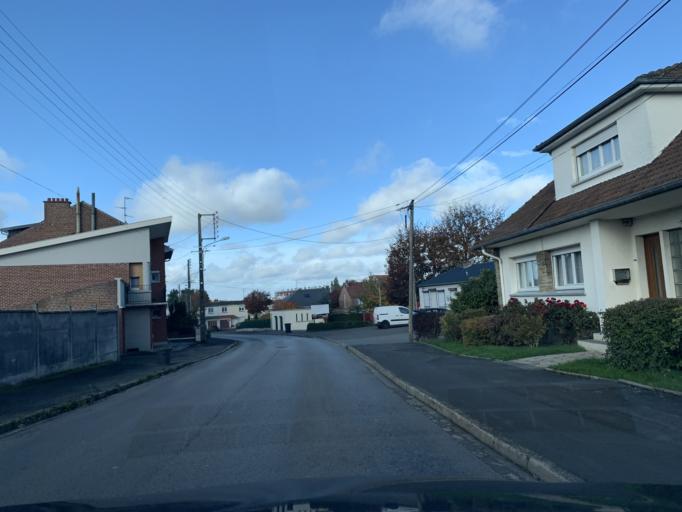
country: FR
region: Nord-Pas-de-Calais
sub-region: Departement du Nord
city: Cambrai
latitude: 50.1822
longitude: 3.2482
